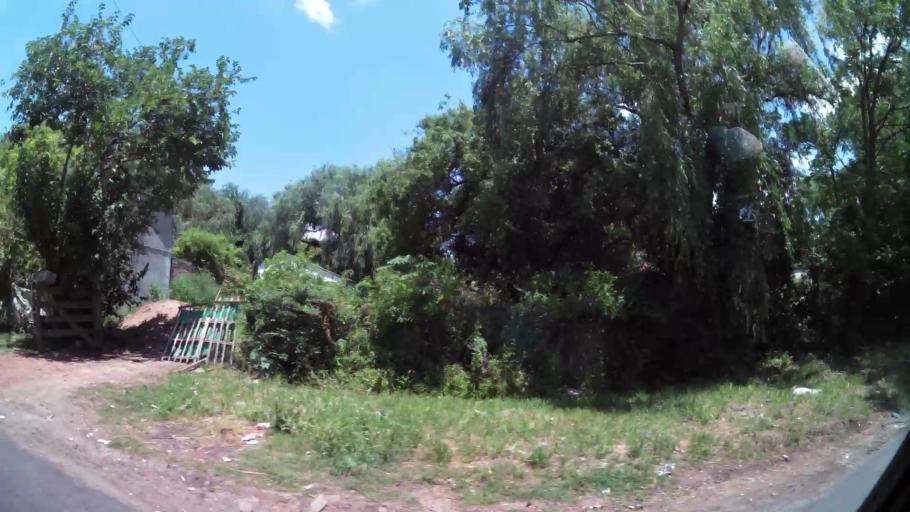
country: AR
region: Buenos Aires
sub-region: Partido de Tigre
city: Tigre
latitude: -34.4257
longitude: -58.5968
